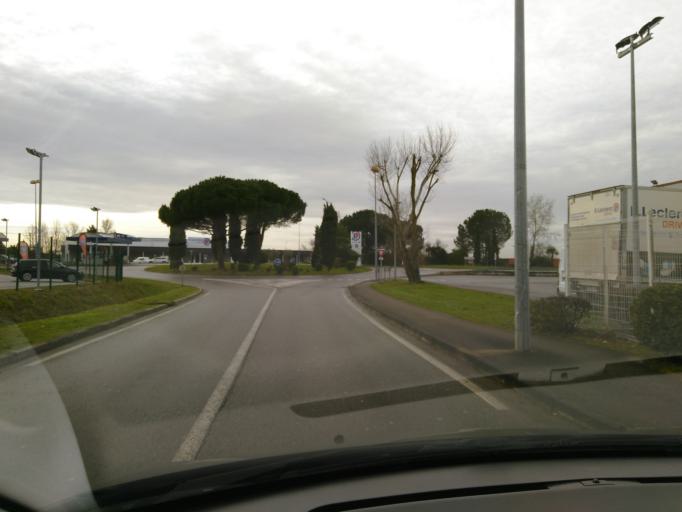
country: FR
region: Midi-Pyrenees
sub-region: Departement de la Haute-Garonne
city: Rouffiac-Tolosan
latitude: 43.6692
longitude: 1.5153
